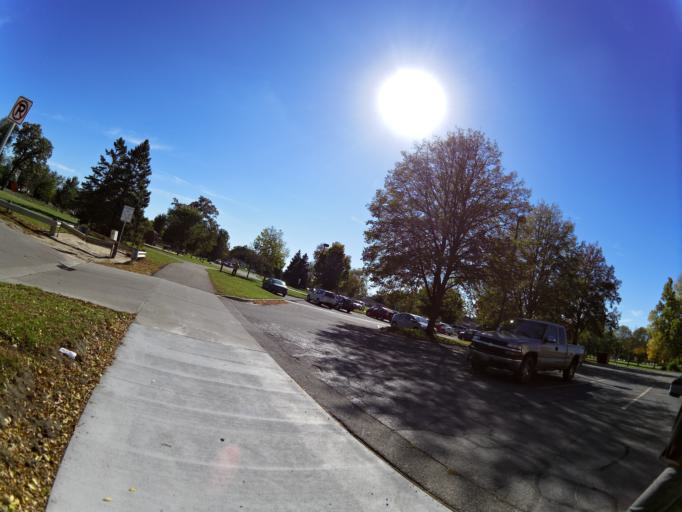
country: US
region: Minnesota
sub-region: Olmsted County
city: Rochester
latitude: 44.0411
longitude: -92.4193
